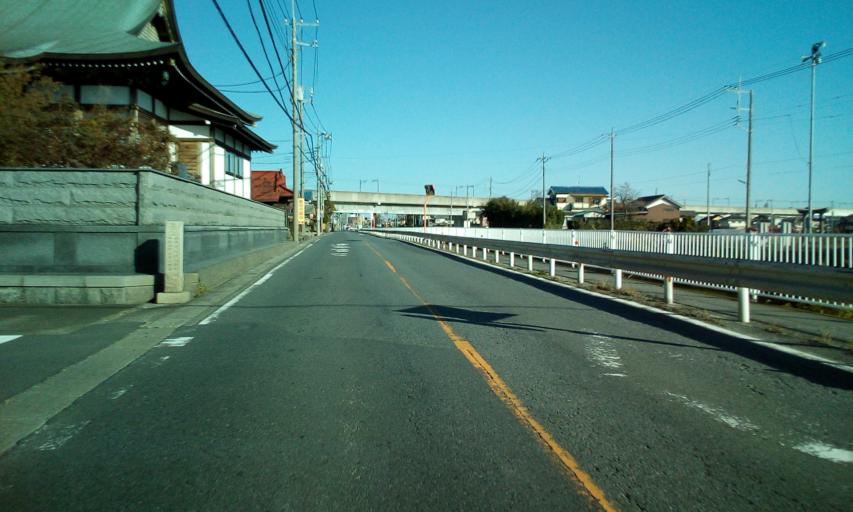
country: JP
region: Chiba
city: Nagareyama
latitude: 35.8282
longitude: 139.8830
